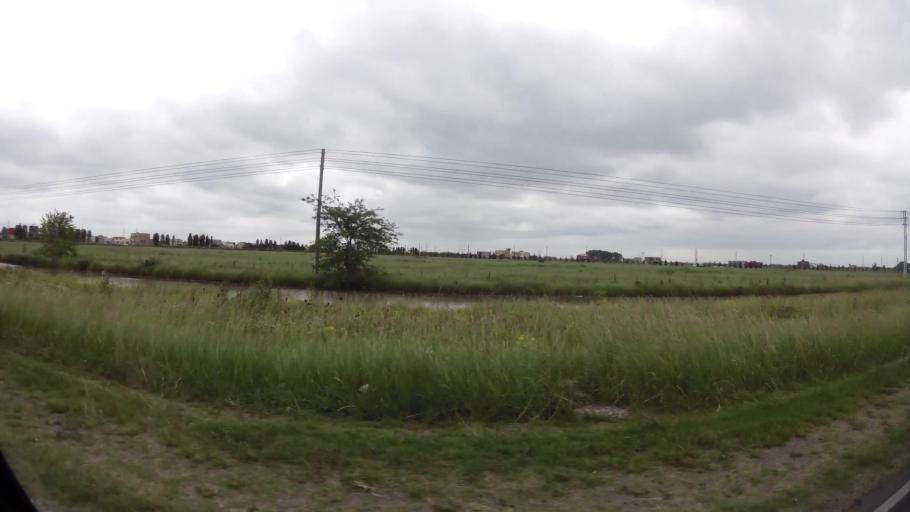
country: AR
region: Buenos Aires
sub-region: Partido de San Vicente
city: San Vicente
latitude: -34.9651
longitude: -58.4664
